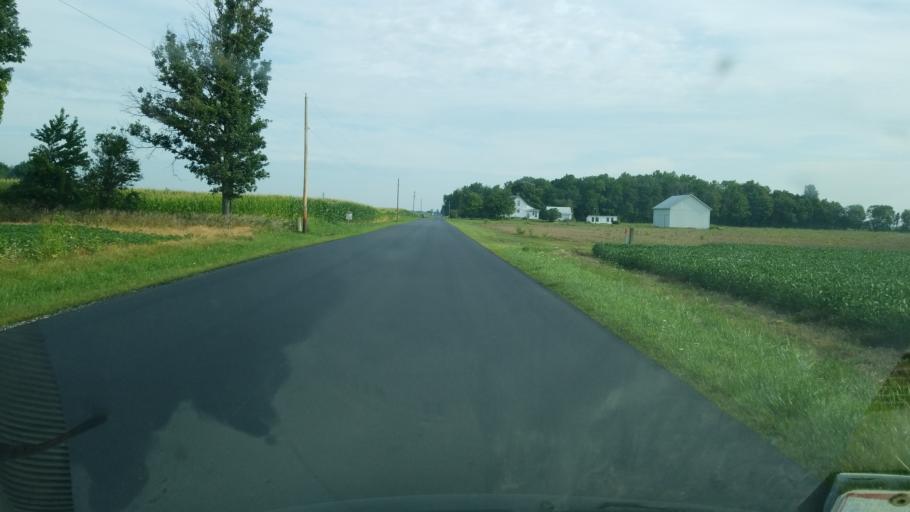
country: US
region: Ohio
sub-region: Crawford County
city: Bucyrus
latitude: 40.8554
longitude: -83.0166
